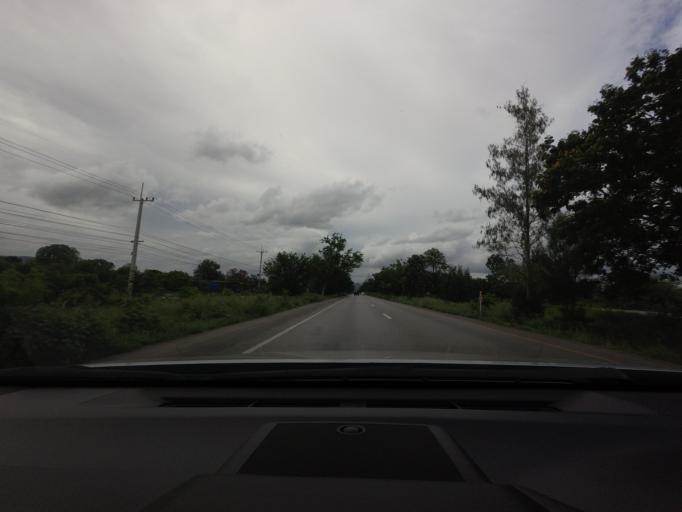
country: TH
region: Phetchaburi
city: Cha-am
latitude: 12.7412
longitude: 99.9293
